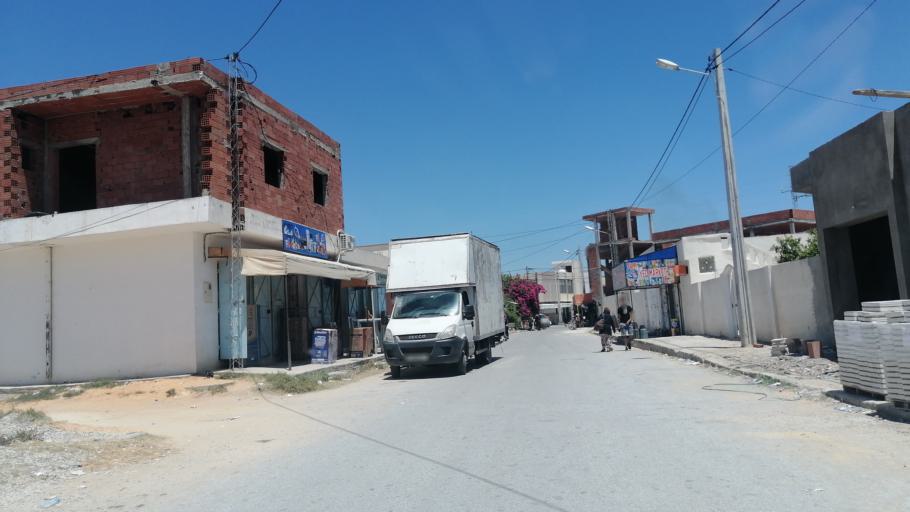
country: TN
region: Al Qayrawan
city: Sbikha
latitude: 36.1198
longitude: 10.0949
